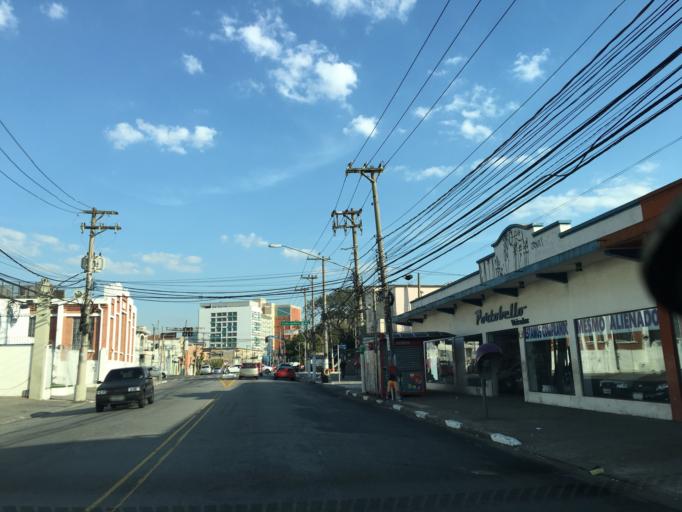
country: BR
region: Sao Paulo
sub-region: Sao Paulo
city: Sao Paulo
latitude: -23.5106
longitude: -46.6262
